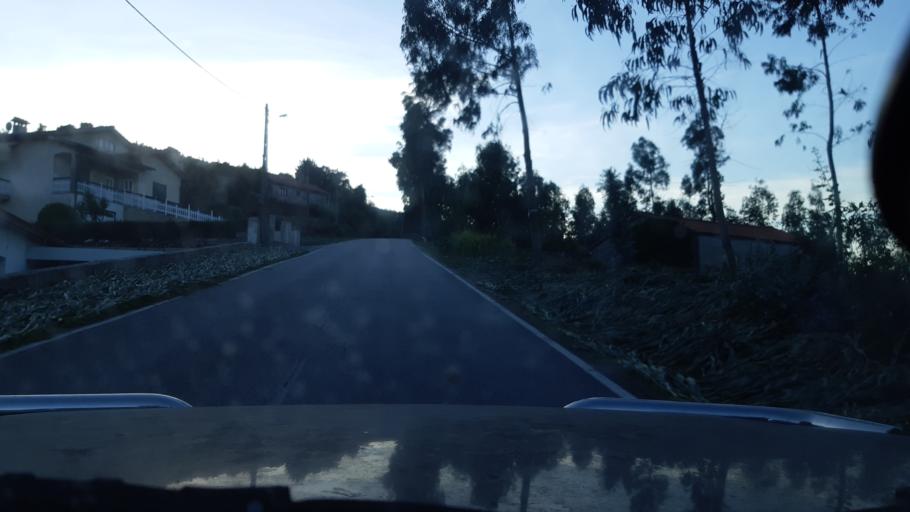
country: PT
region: Viseu
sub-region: Mortagua
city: Mortagua
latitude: 40.5433
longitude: -8.2753
